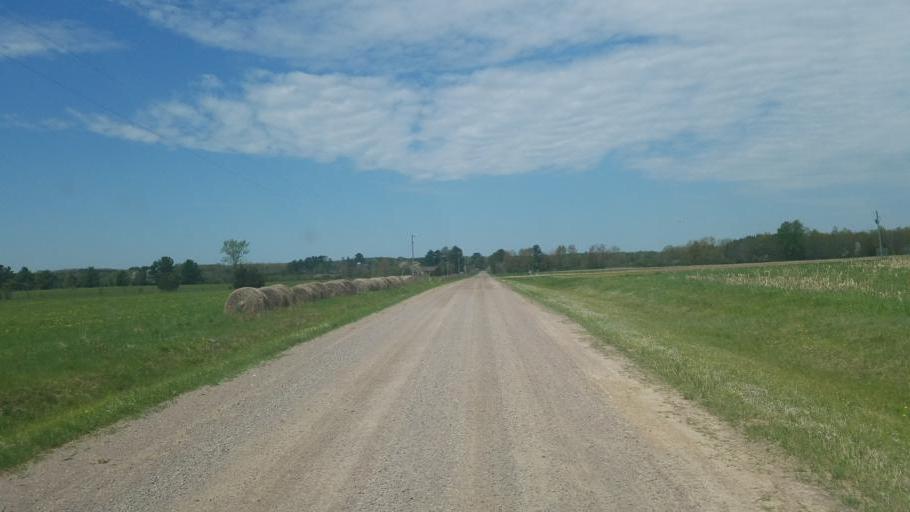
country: US
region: Wisconsin
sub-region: Clark County
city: Neillsville
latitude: 44.4732
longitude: -90.4567
